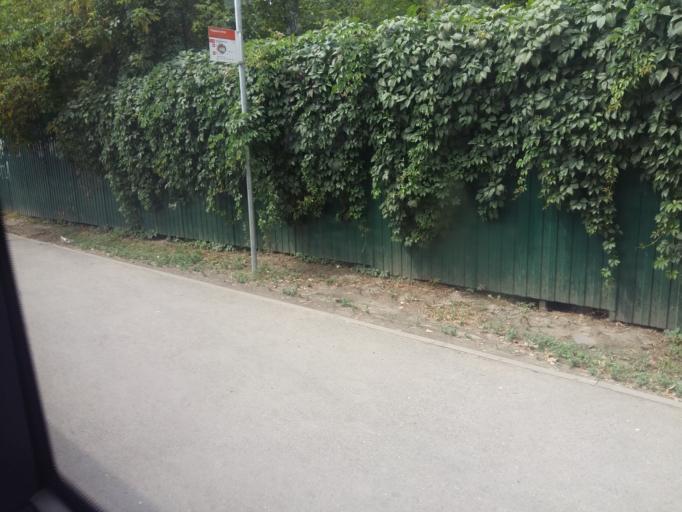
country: RU
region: Rostov
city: Imeni Chkalova
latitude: 47.2861
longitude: 39.7572
